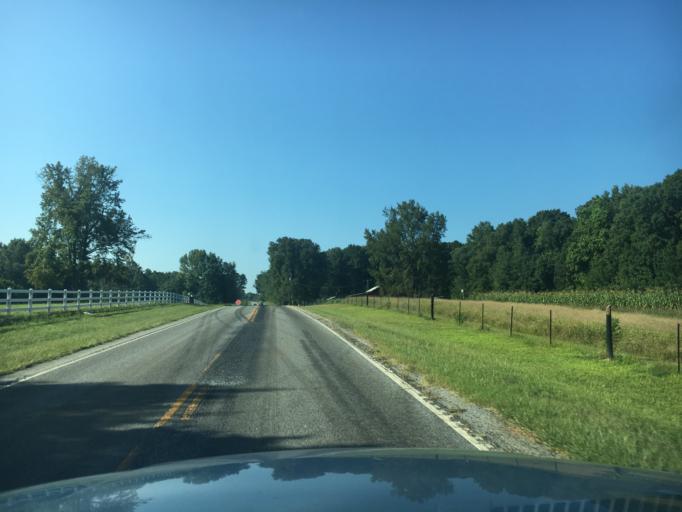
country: US
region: South Carolina
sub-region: Anderson County
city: Williamston
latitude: 34.6012
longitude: -82.3482
